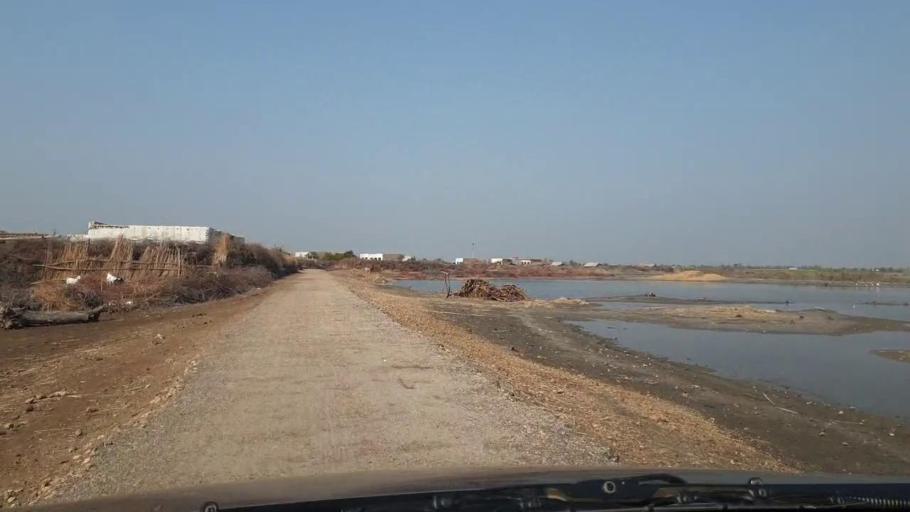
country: PK
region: Sindh
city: Jhol
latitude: 25.9037
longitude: 69.0007
